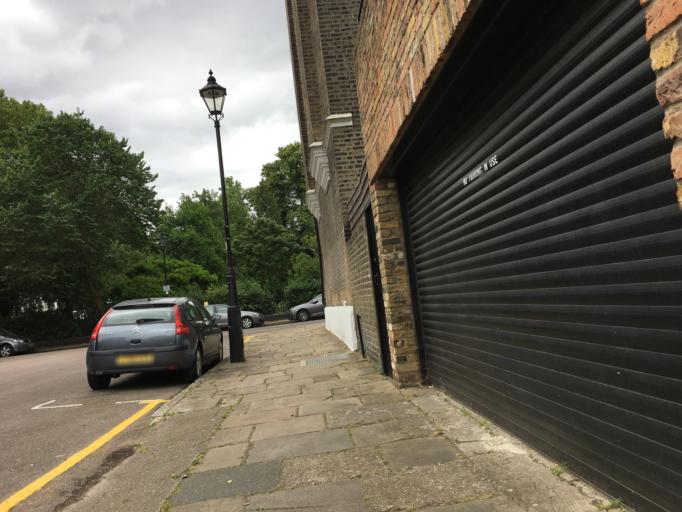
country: GB
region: England
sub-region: Greater London
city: Islington
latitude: 51.5402
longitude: -0.1086
